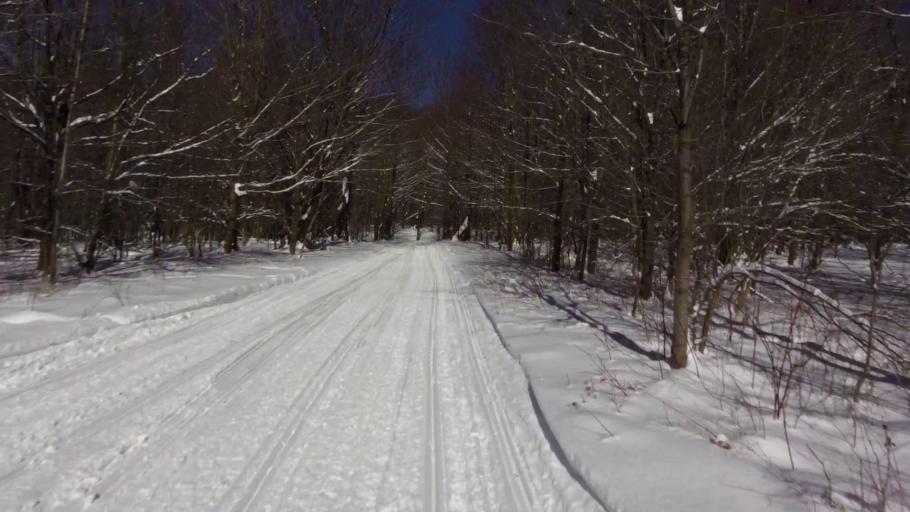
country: US
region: New York
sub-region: Chautauqua County
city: Mayville
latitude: 42.2696
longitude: -79.4549
